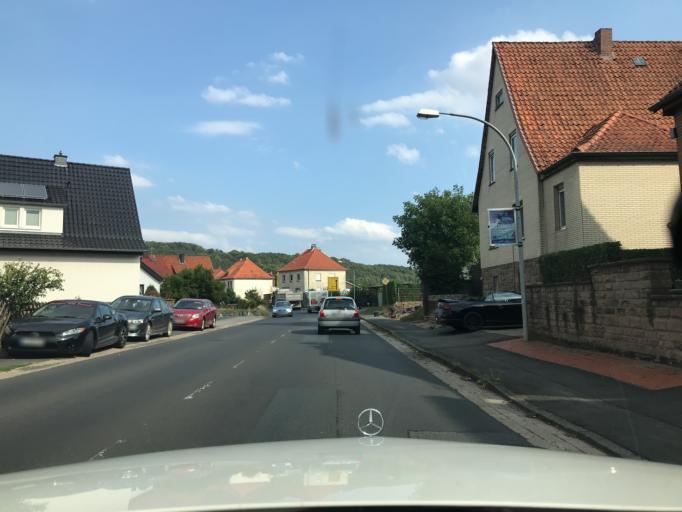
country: DE
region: Lower Saxony
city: Adelebsen
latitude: 51.5947
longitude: 9.7799
